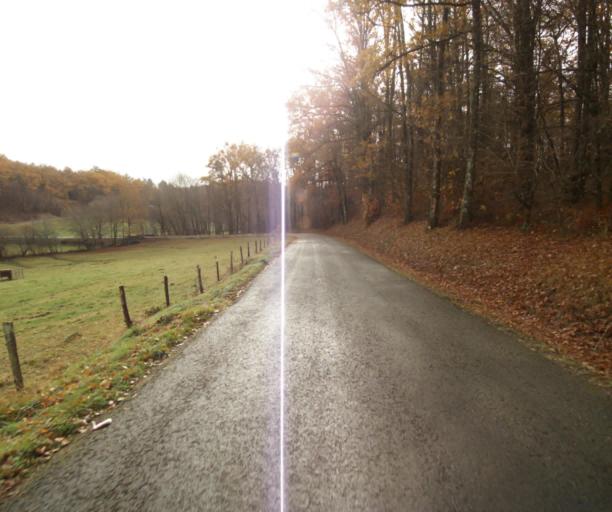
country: FR
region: Limousin
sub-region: Departement de la Correze
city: Saint-Mexant
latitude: 45.2346
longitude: 1.6415
